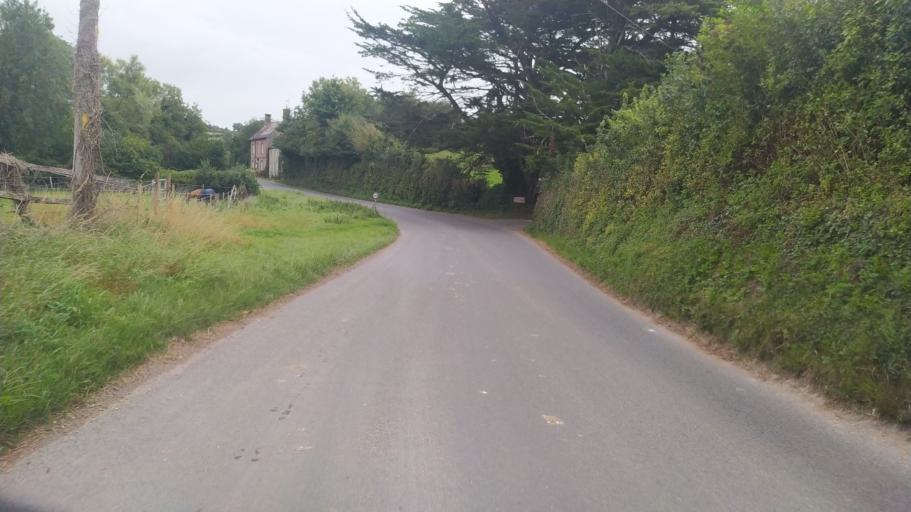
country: GB
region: England
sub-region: Dorset
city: Dorchester
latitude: 50.7906
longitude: -2.4154
